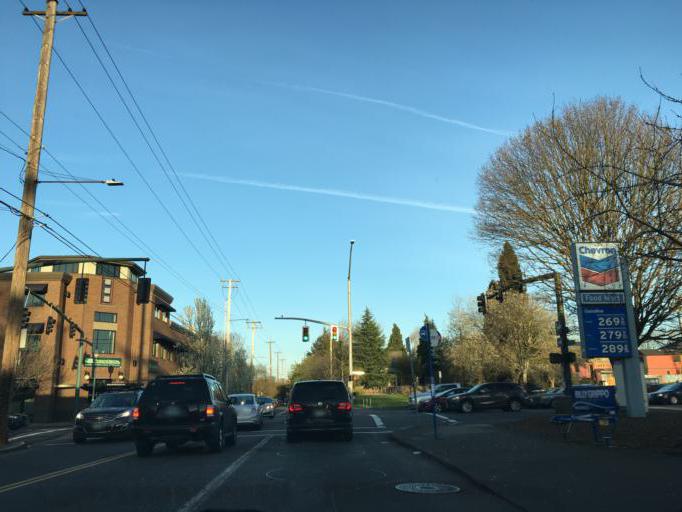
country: US
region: Oregon
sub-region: Multnomah County
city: Portland
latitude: 45.5482
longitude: -122.6621
